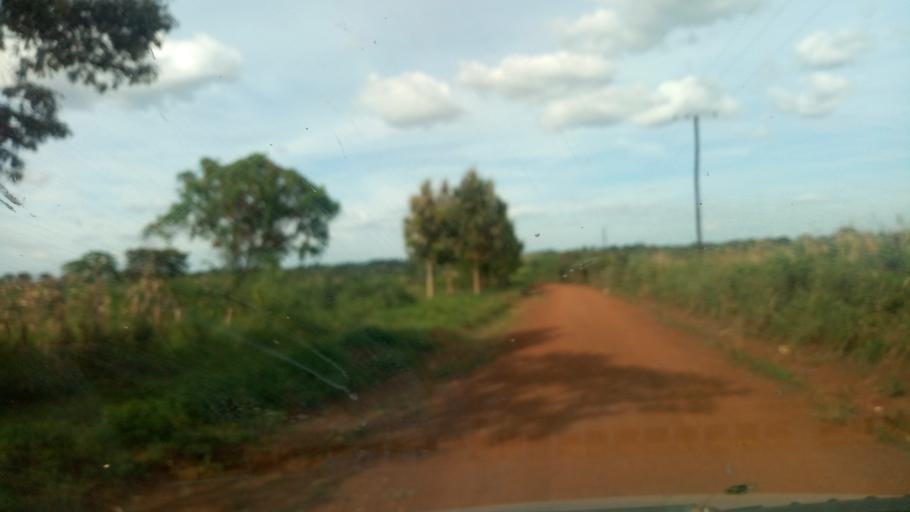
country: UG
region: Western Region
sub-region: Kiryandongo District
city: Kiryandongo
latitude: 1.8159
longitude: 31.9330
